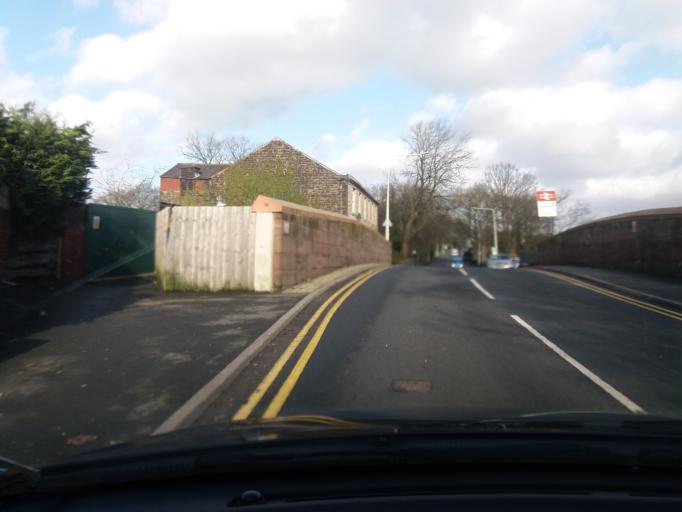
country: GB
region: England
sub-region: Lancashire
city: Adlington
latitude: 53.6133
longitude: -2.6035
